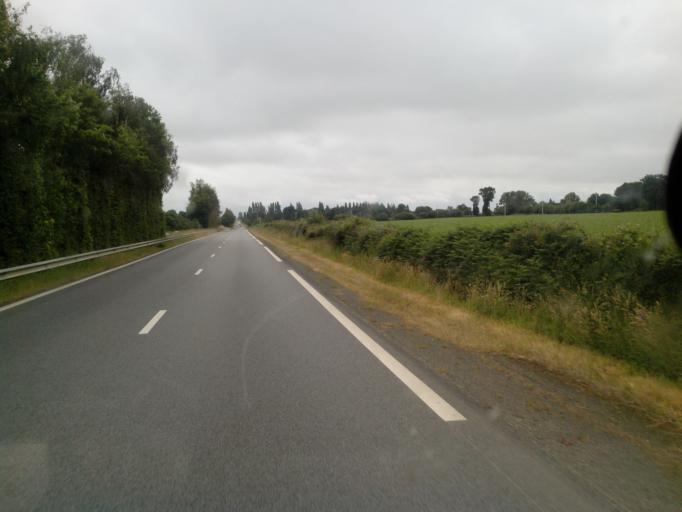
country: FR
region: Brittany
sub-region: Departement d'Ille-et-Vilaine
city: Chevaigne
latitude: 48.2319
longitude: -1.6223
